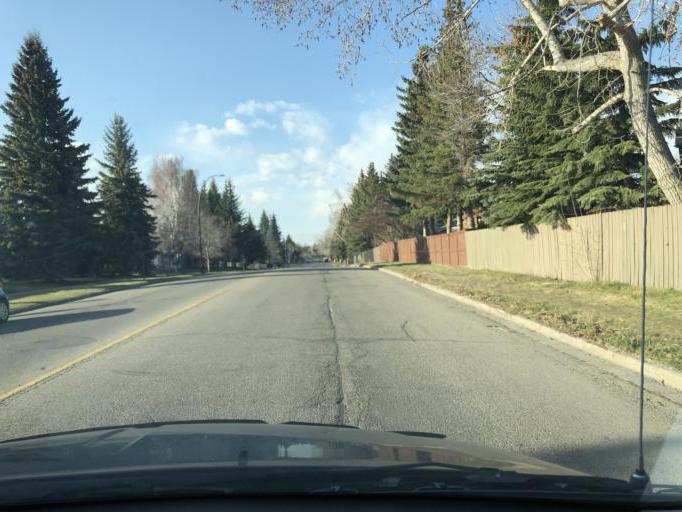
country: CA
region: Alberta
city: Calgary
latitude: 50.9669
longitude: -114.1063
